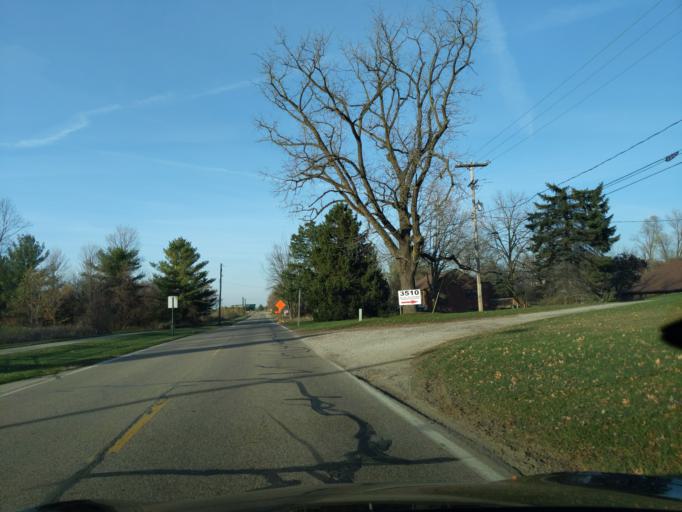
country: US
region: Michigan
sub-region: Ingham County
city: East Lansing
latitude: 42.7689
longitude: -84.5083
